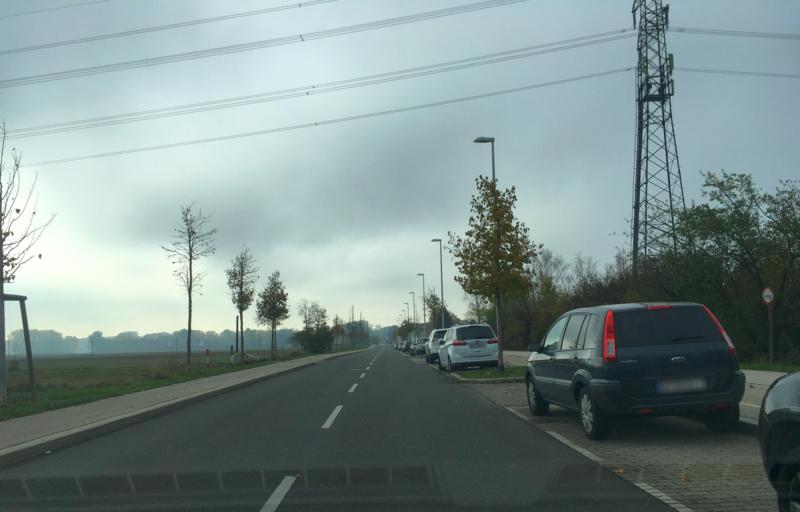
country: AT
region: Lower Austria
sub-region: Politischer Bezirk Ganserndorf
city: Gross-Enzersdorf
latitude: 48.2112
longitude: 16.4899
